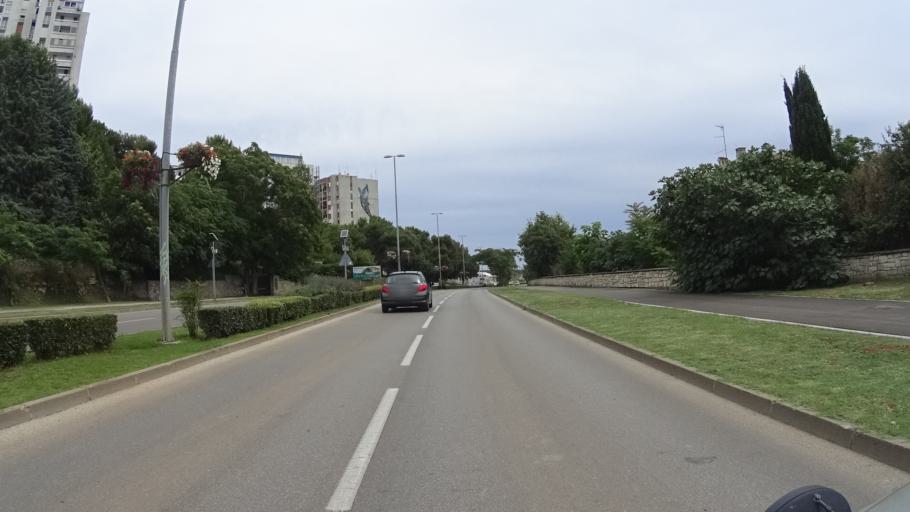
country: HR
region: Istarska
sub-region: Grad Pula
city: Pula
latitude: 44.8528
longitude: 13.8398
